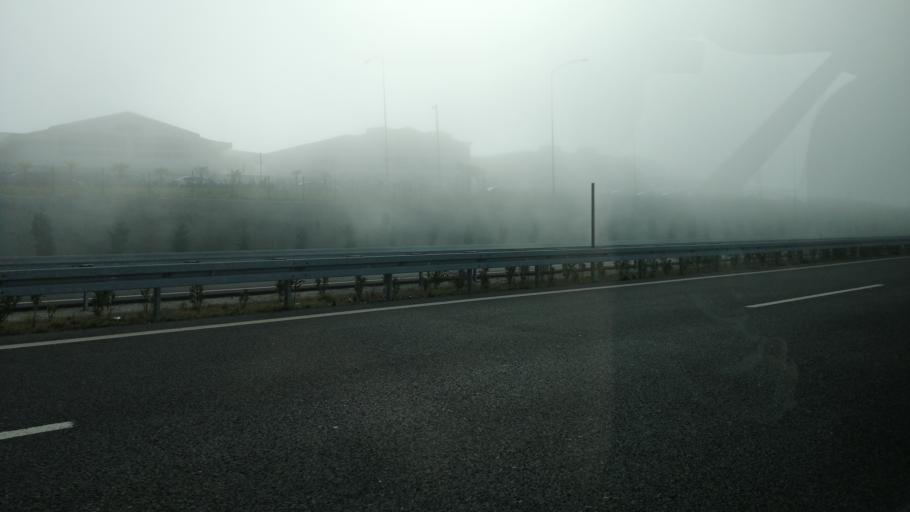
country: TR
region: Kocaeli
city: Tavsanli
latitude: 40.7735
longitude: 29.5184
